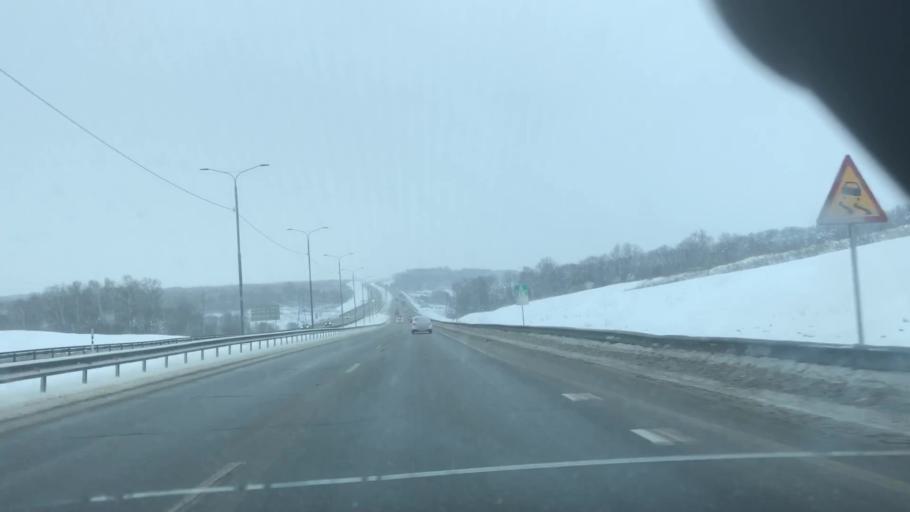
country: RU
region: Moskovskaya
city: Stupino
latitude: 54.8055
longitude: 38.0744
